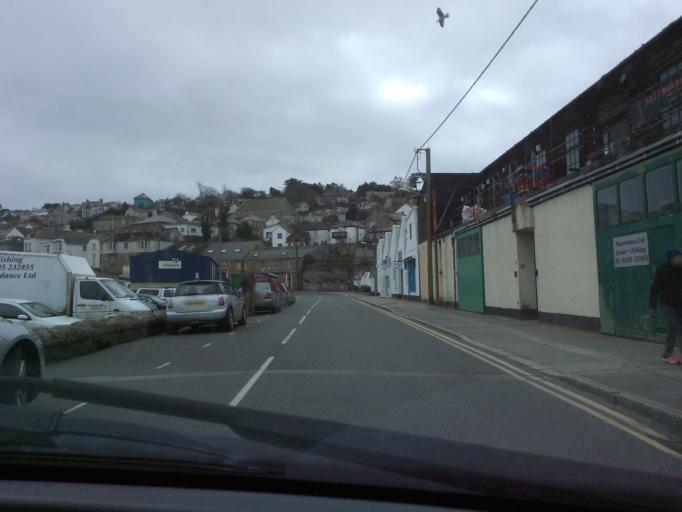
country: GB
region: England
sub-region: Cornwall
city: Penzance
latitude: 50.1041
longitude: -5.5495
